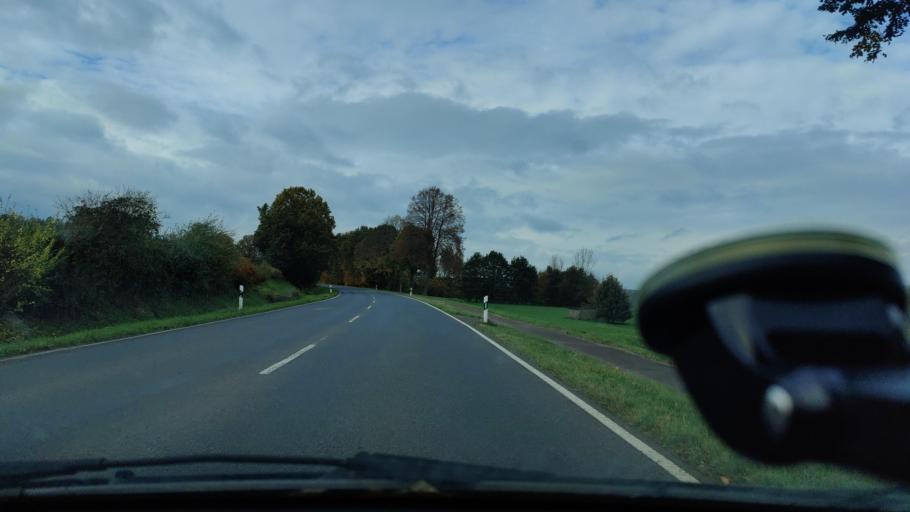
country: DE
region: North Rhine-Westphalia
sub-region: Regierungsbezirk Dusseldorf
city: Sonsbeck
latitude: 51.6356
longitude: 6.4016
